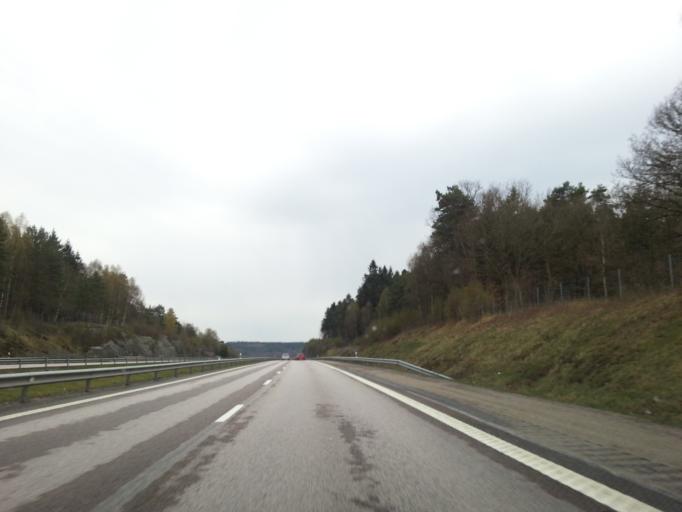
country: SE
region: Halland
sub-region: Kungsbacka Kommun
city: Frillesas
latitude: 57.3359
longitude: 12.2057
